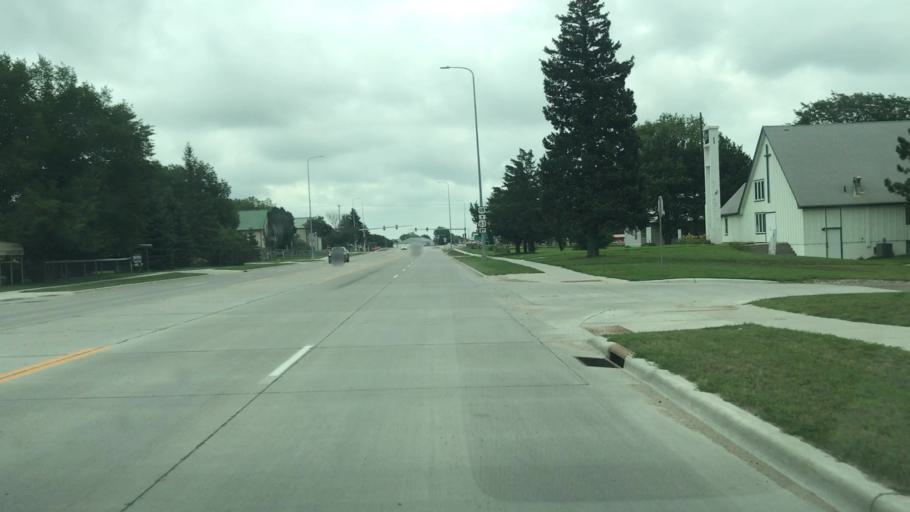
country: US
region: South Dakota
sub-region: Todd County
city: Mission
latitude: 43.3057
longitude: -100.6558
